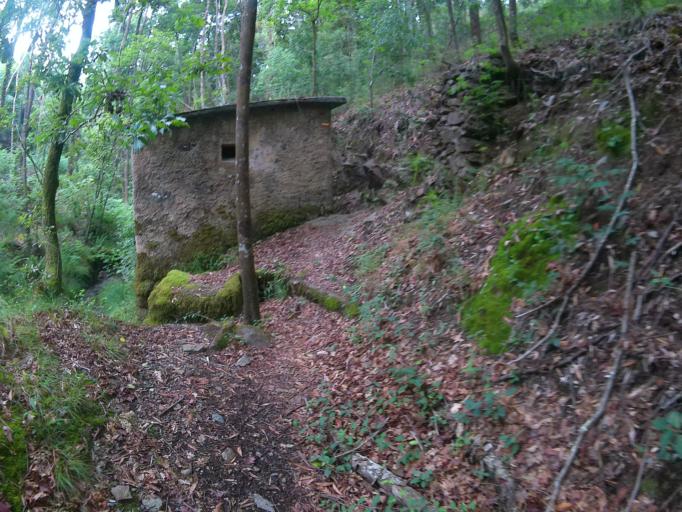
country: PT
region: Aveiro
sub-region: Albergaria-A-Velha
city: Branca
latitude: 40.7692
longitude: -8.4391
